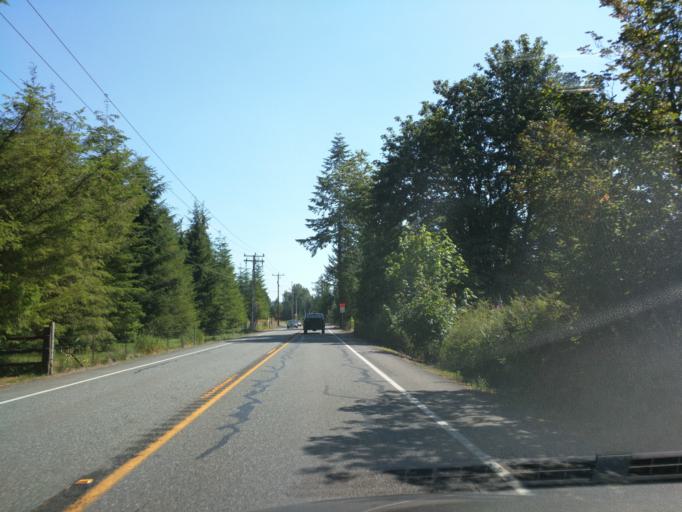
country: US
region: Washington
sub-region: Whatcom County
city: Peaceful Valley
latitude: 48.9188
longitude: -122.1433
